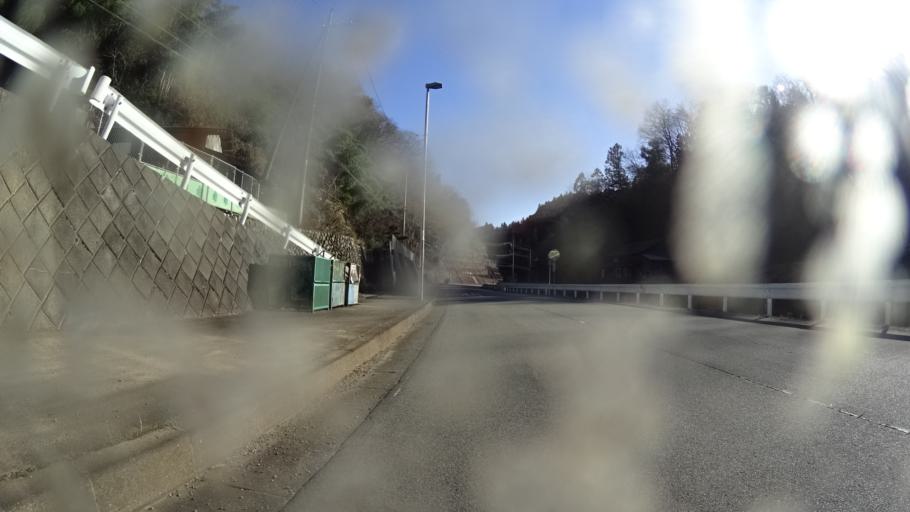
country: JP
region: Yamanashi
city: Uenohara
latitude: 35.6328
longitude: 139.1421
